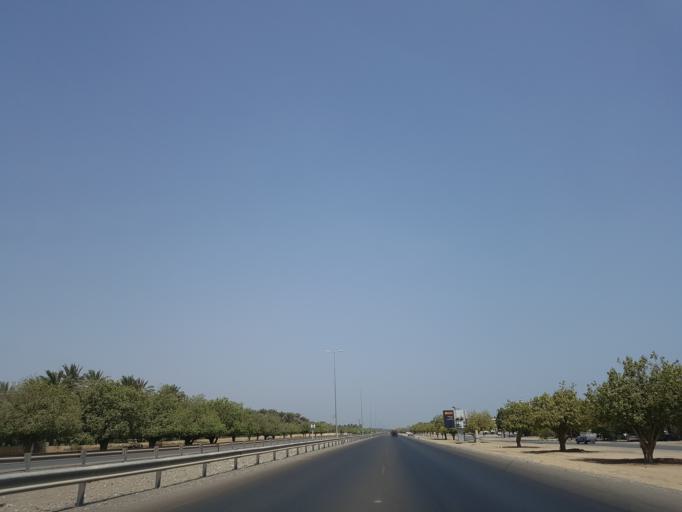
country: OM
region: Al Batinah
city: Saham
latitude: 24.1639
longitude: 56.8630
